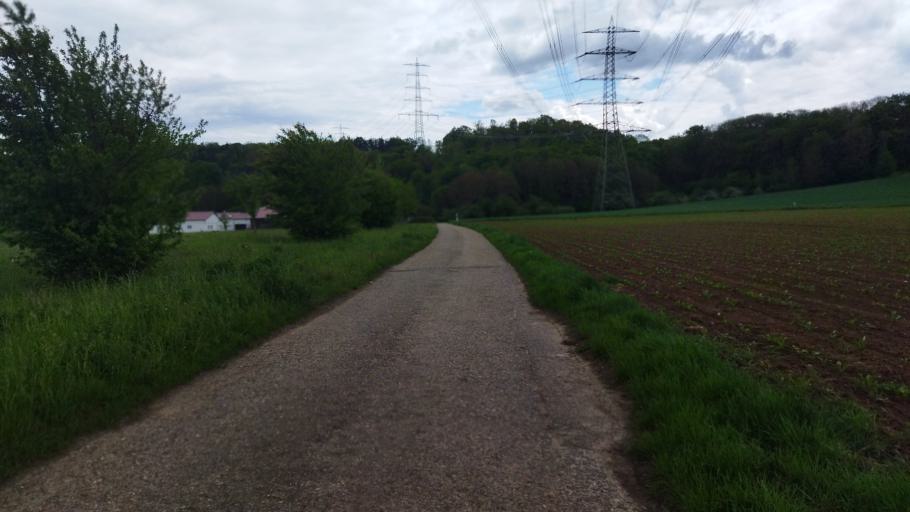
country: DE
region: Baden-Wuerttemberg
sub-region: Regierungsbezirk Stuttgart
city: Neckarwestheim
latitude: 49.0375
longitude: 9.1763
